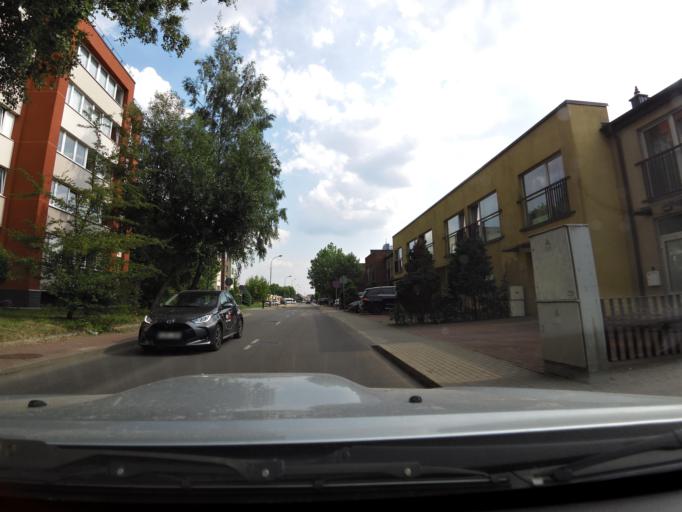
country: LT
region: Klaipedos apskritis
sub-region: Klaipeda
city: Klaipeda
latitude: 55.6971
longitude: 21.1437
